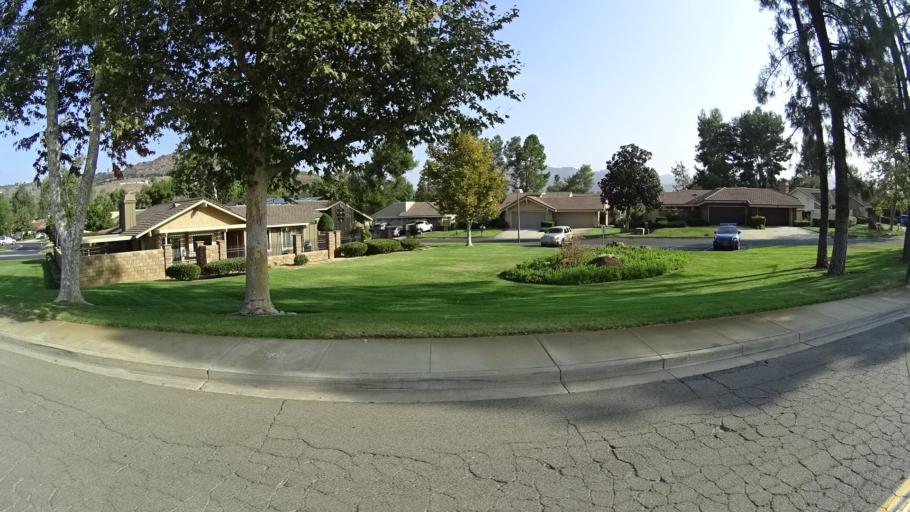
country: US
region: California
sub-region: San Diego County
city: Rainbow
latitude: 33.3416
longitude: -117.1613
